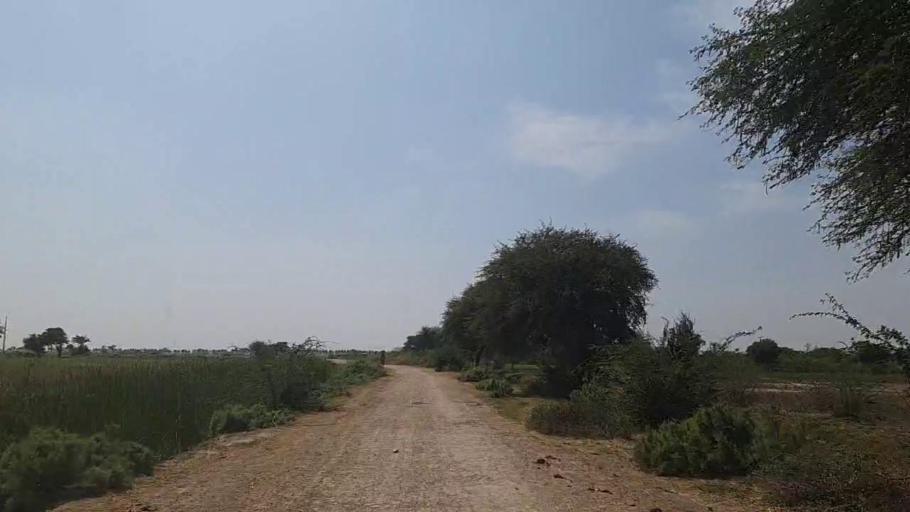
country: PK
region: Sindh
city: Jati
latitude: 24.5345
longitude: 68.2979
